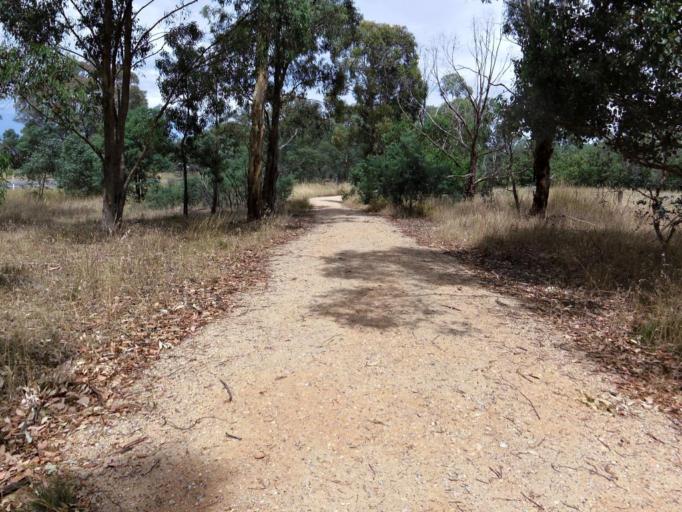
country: AU
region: Victoria
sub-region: Greater Bendigo
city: Kennington
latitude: -36.8749
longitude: 144.6358
